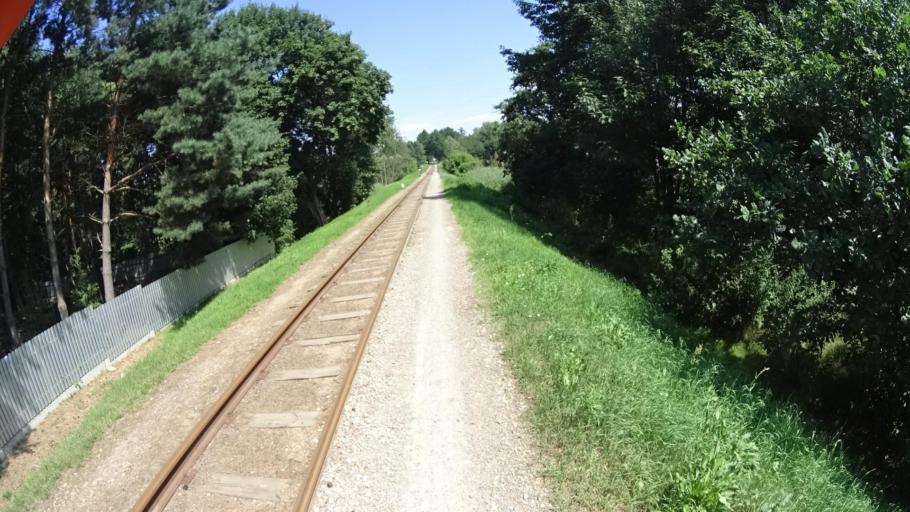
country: PL
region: Masovian Voivodeship
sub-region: Powiat piaseczynski
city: Lesznowola
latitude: 52.0320
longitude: 20.9549
